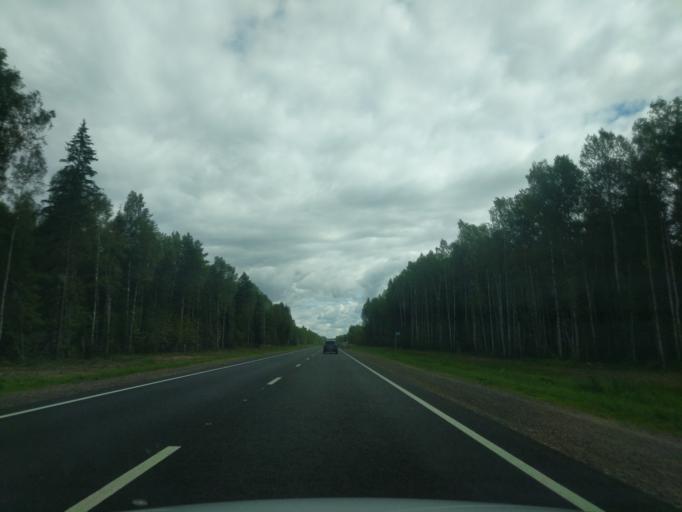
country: RU
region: Jaroslavl
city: Tunoshna
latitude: 57.5561
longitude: 40.2099
